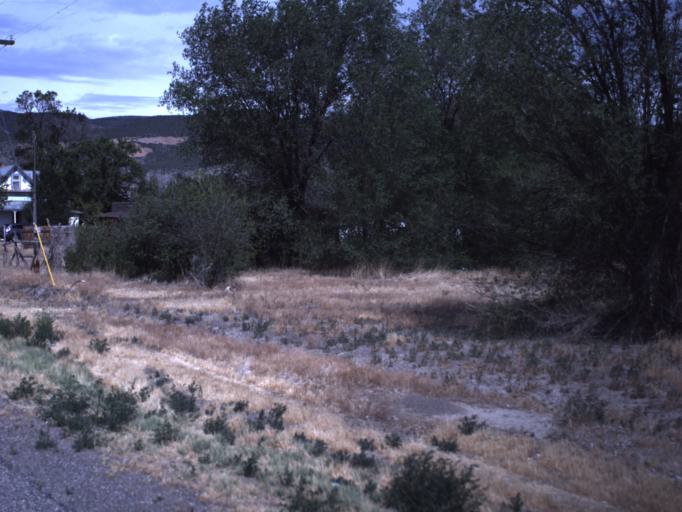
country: US
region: Utah
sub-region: Sevier County
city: Monroe
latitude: 38.6243
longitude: -112.2168
